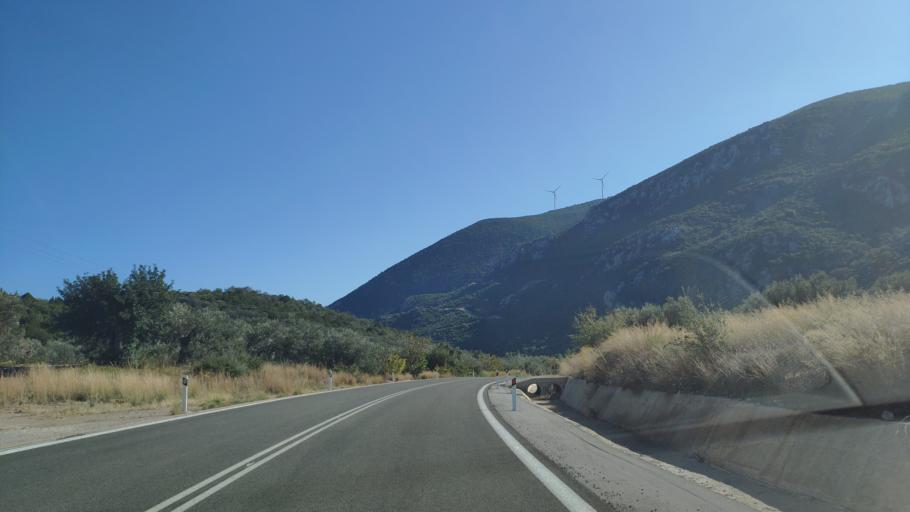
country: GR
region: Peloponnese
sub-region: Nomos Argolidos
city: Palaia Epidavros
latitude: 37.5621
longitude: 23.2564
